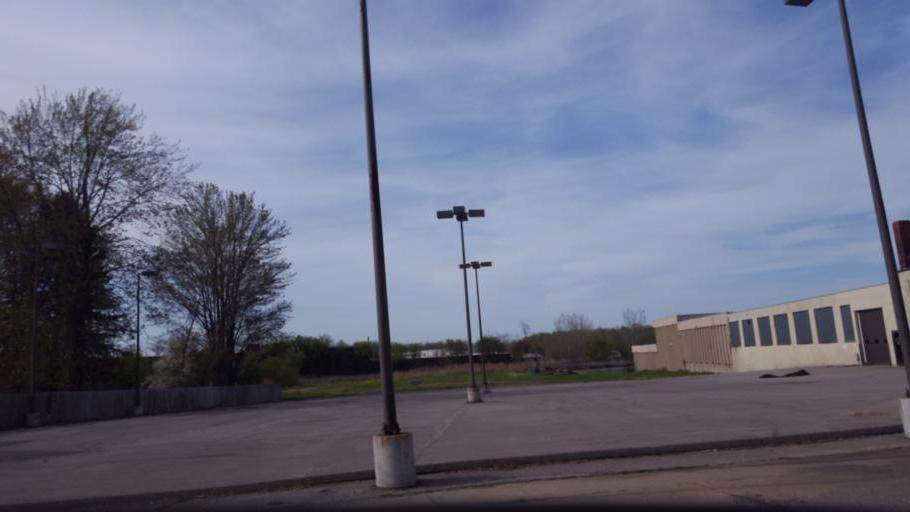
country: US
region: Ohio
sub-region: Ashtabula County
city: Geneva
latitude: 41.8081
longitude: -80.9399
